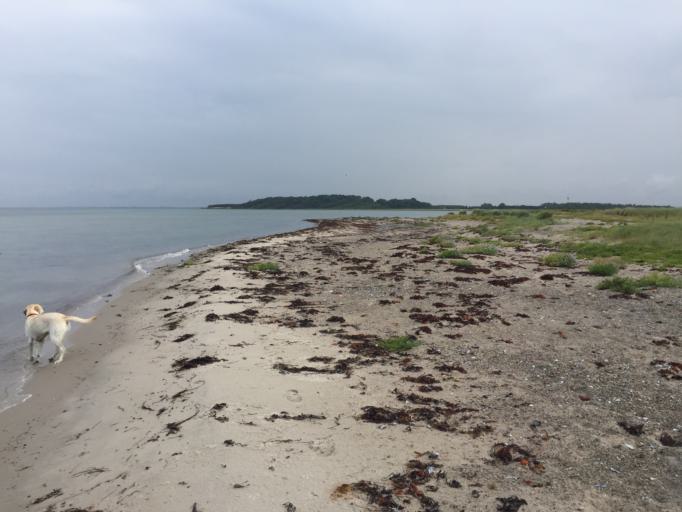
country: DK
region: Zealand
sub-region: Slagelse Kommune
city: Korsor
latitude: 55.2359
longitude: 11.1708
